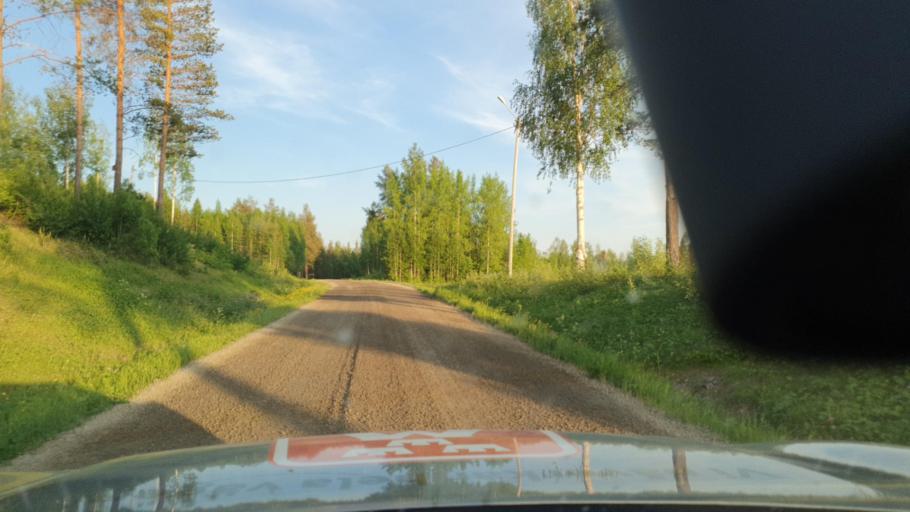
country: SE
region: Norrbotten
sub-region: Bodens Kommun
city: Boden
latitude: 66.1931
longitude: 21.4991
